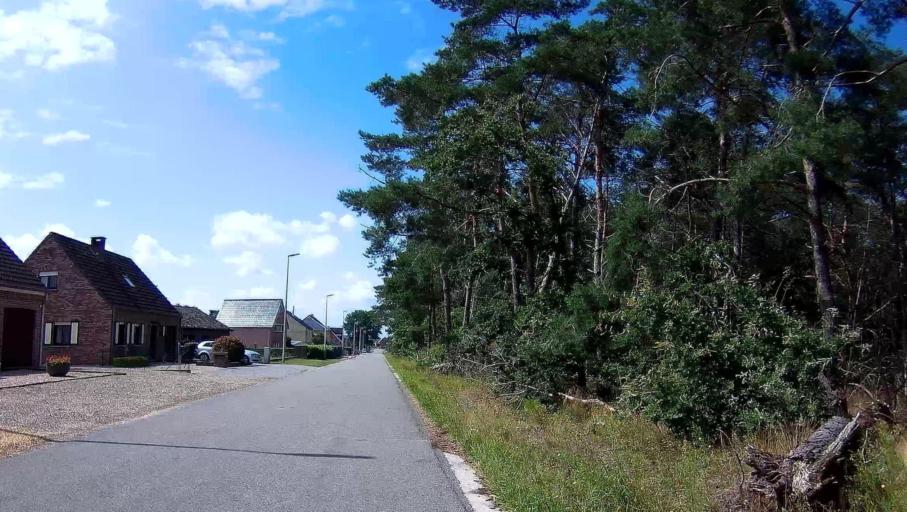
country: BE
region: Flanders
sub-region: Provincie Limburg
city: Leopoldsburg
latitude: 51.1652
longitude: 5.2909
